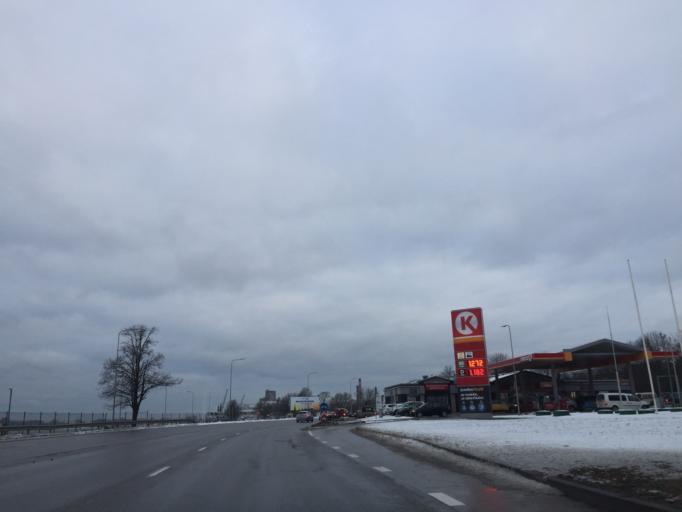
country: LV
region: Riga
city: Riga
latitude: 56.9546
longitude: 24.0972
